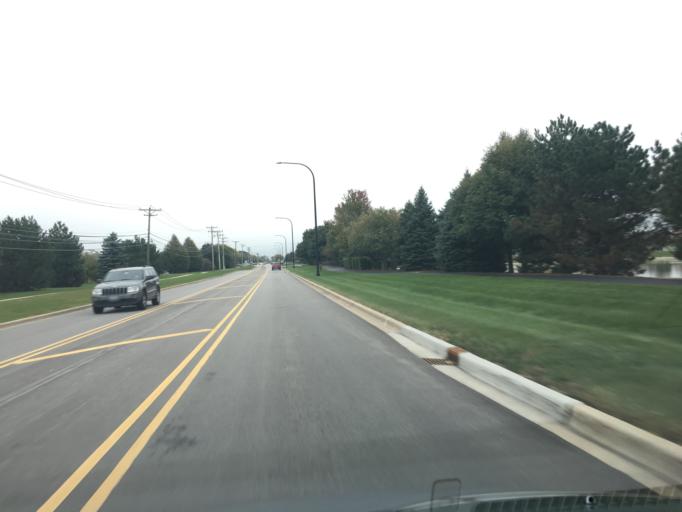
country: US
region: Illinois
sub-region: Will County
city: Plainfield
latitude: 41.6515
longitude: -88.2102
